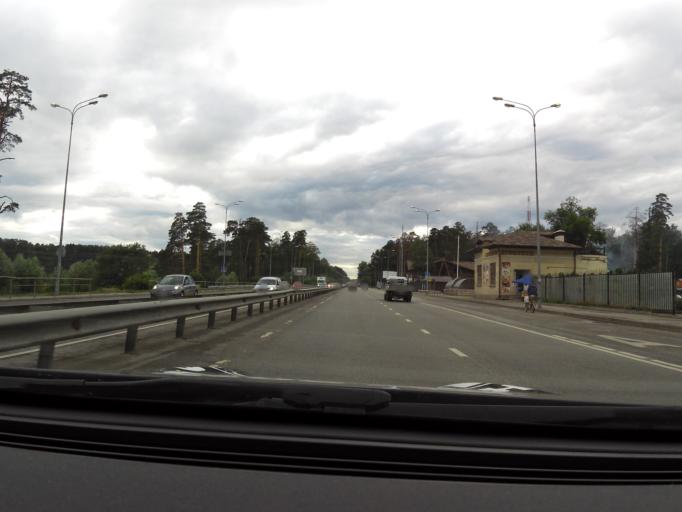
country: RU
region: Tatarstan
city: Staroye Arakchino
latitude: 55.8377
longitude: 48.9660
